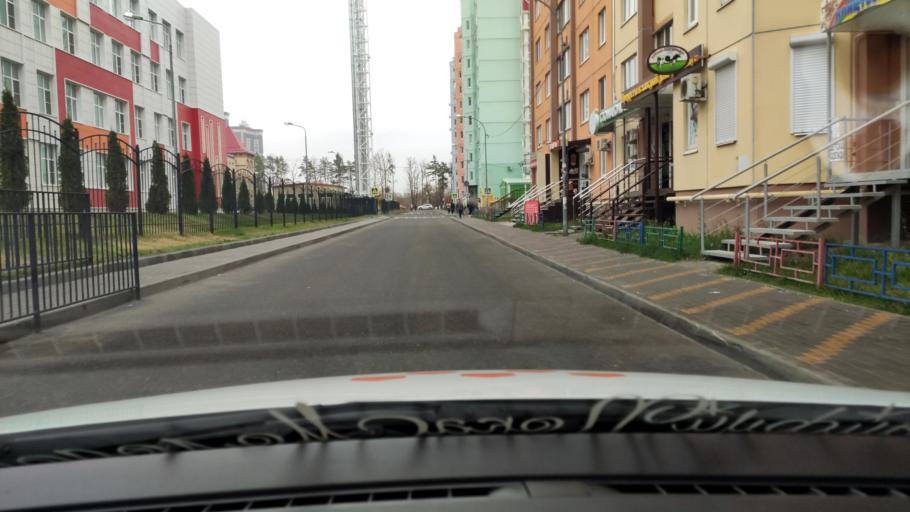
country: RU
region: Voronezj
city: Podgornoye
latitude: 51.7151
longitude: 39.1848
